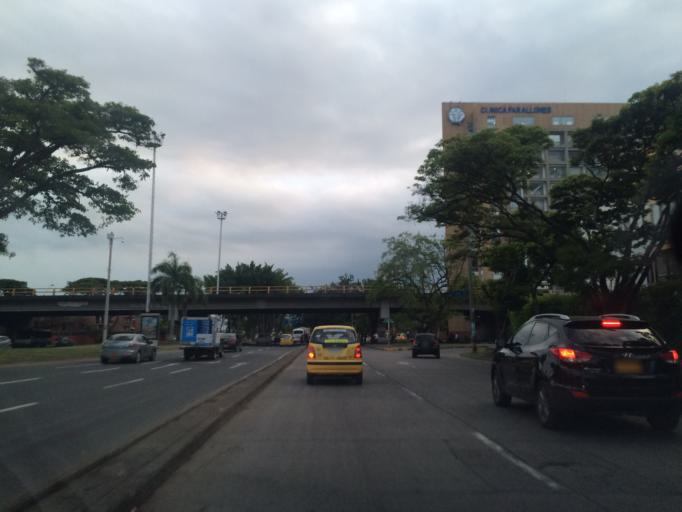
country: CO
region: Valle del Cauca
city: Cali
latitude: 3.4112
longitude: -76.5386
